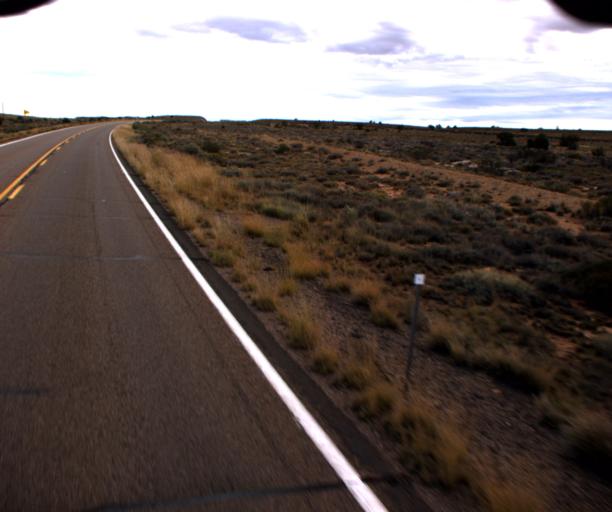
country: US
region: Arizona
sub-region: Navajo County
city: Holbrook
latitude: 34.8527
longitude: -110.1491
